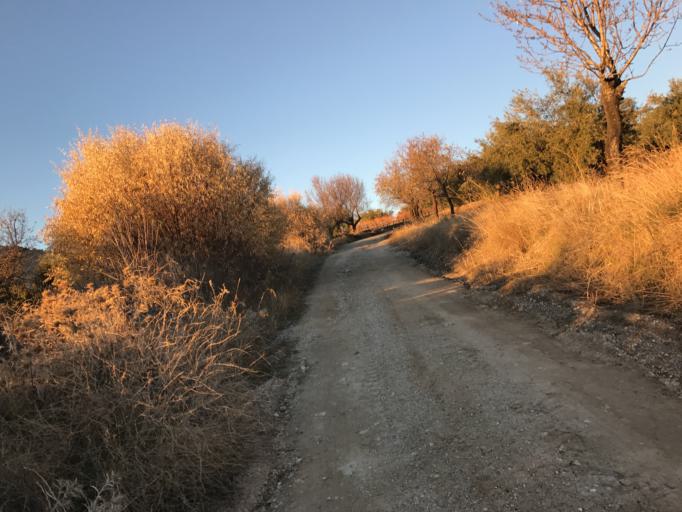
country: ES
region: Andalusia
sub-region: Provincia de Granada
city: Beas de Granada
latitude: 37.2242
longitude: -3.4729
